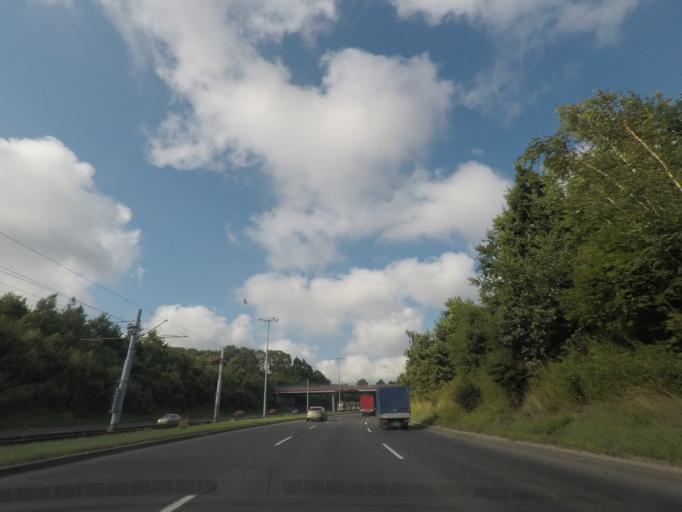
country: PL
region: Pomeranian Voivodeship
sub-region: Gdansk
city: Gdansk
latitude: 54.3464
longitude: 18.6309
